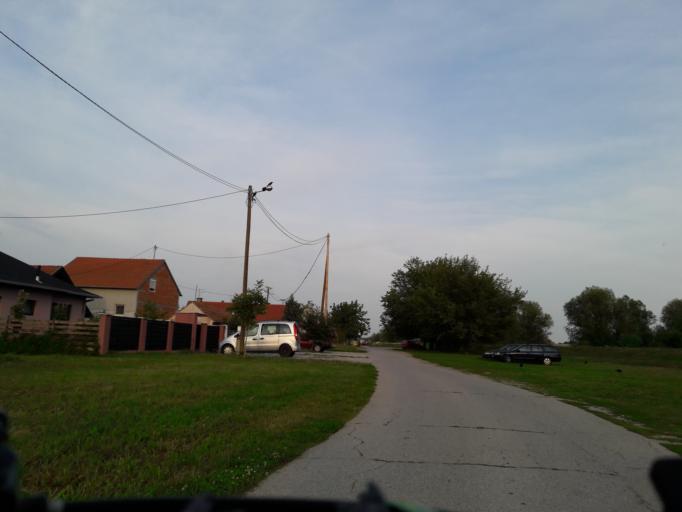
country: HR
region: Osjecko-Baranjska
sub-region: Grad Osijek
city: Osijek
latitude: 45.5616
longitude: 18.7066
